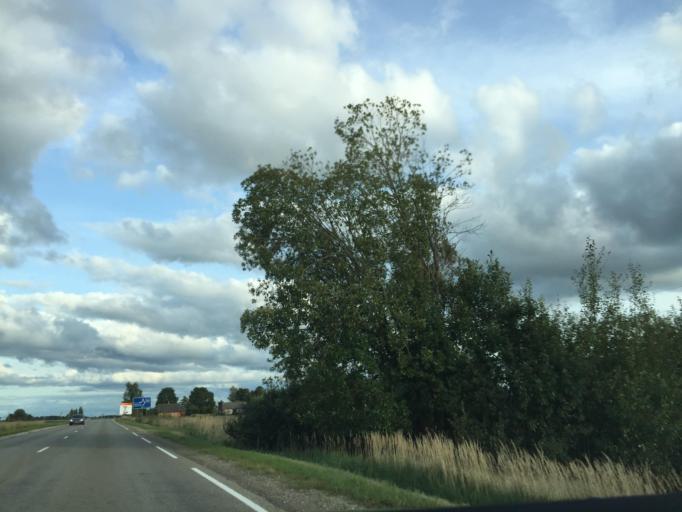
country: LV
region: Nereta
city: Nereta
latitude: 56.2542
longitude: 25.2109
